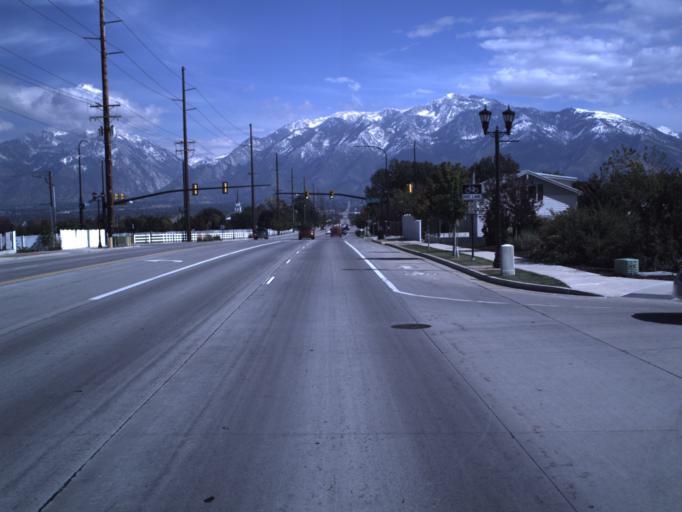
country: US
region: Utah
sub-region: Salt Lake County
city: South Jordan Heights
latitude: 40.5441
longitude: -111.9496
